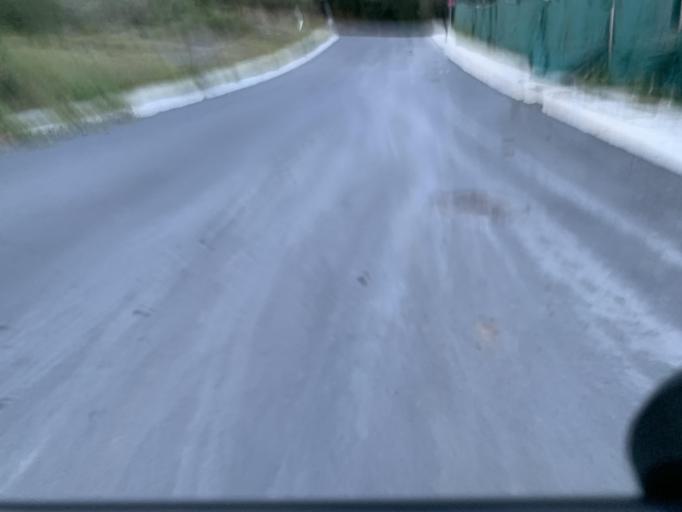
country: MX
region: Nuevo Leon
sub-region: Juarez
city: Bosques de San Pedro
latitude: 25.5245
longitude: -100.1923
